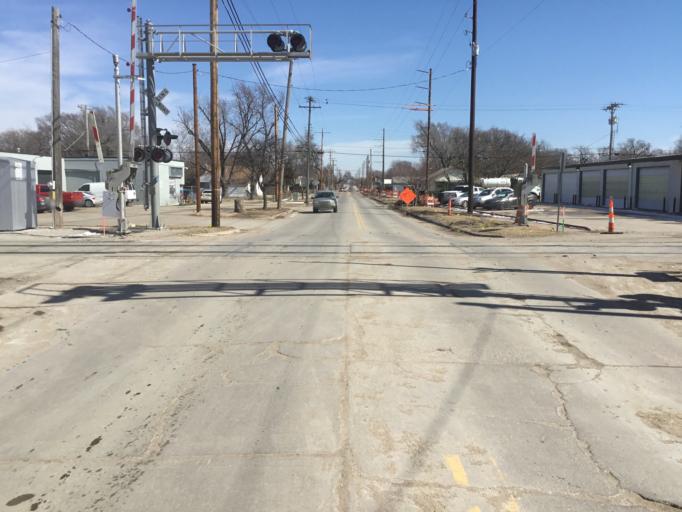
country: US
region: Kansas
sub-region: Sedgwick County
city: Wichita
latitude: 37.6571
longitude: -97.3291
